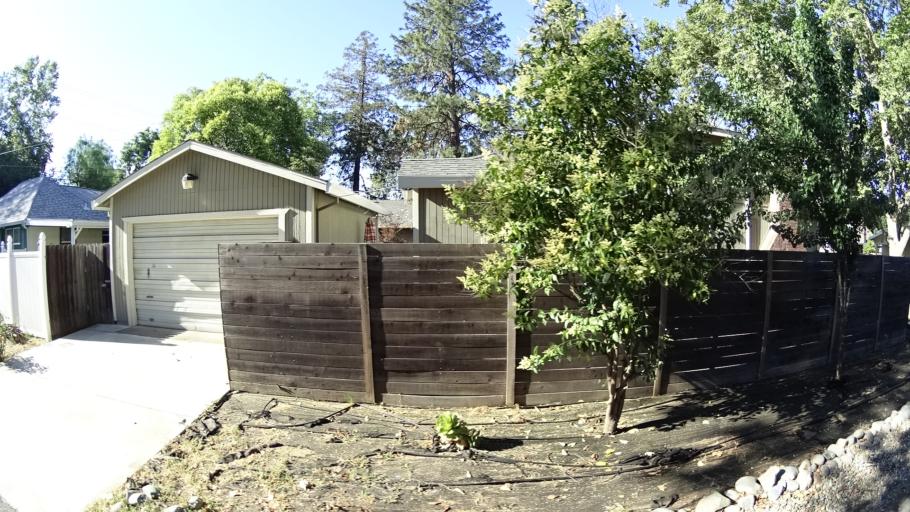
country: US
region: California
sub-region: Sacramento County
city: Parkway
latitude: 38.5330
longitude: -121.4419
